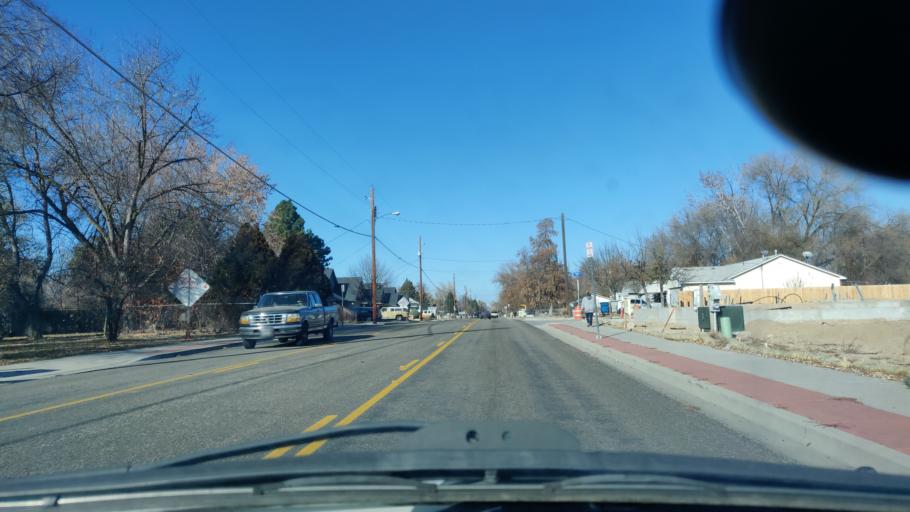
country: US
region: Idaho
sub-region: Ada County
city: Garden City
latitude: 43.6385
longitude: -116.2527
